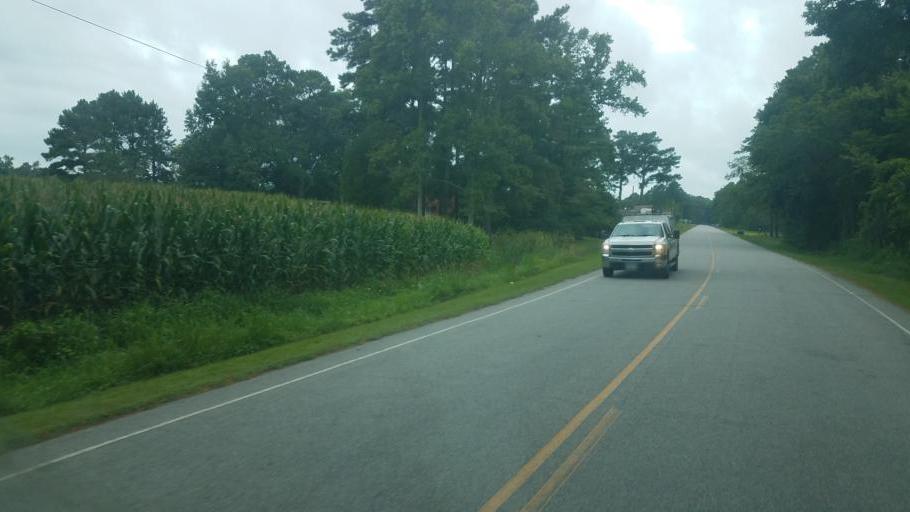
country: US
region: North Carolina
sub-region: Tyrrell County
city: Columbia
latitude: 35.9139
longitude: -76.2852
